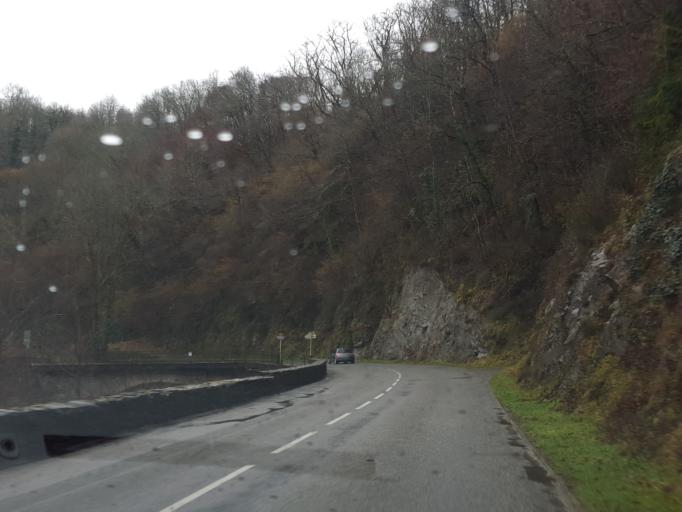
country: FR
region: Midi-Pyrenees
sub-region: Departement de l'Ariege
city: Saint-Girons
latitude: 42.8998
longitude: 1.2301
